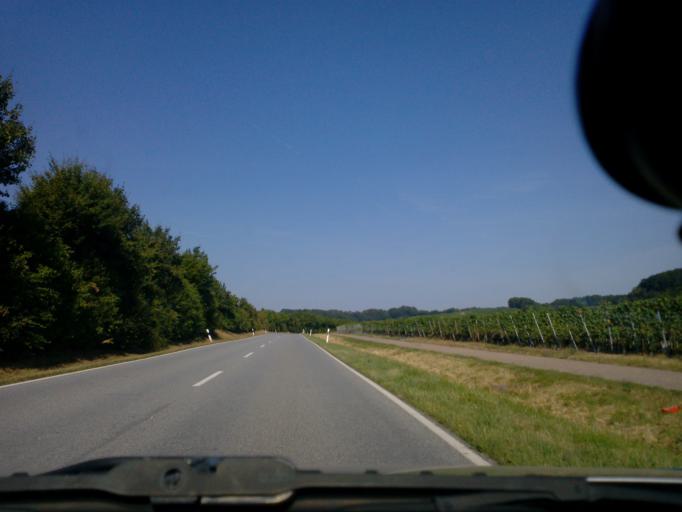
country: DE
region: Baden-Wuerttemberg
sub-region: Regierungsbezirk Stuttgart
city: Brackenheim
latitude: 49.0970
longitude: 9.0348
